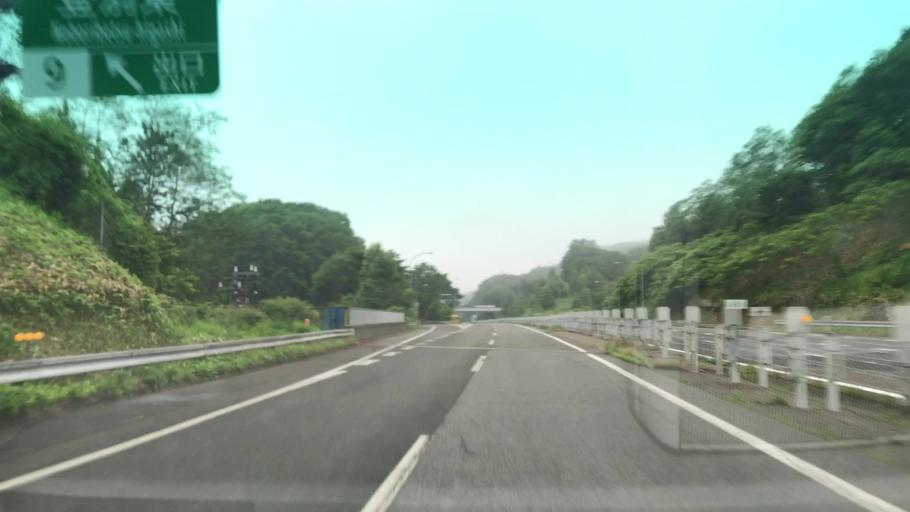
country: JP
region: Hokkaido
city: Shiraoi
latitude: 42.4636
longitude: 141.1780
